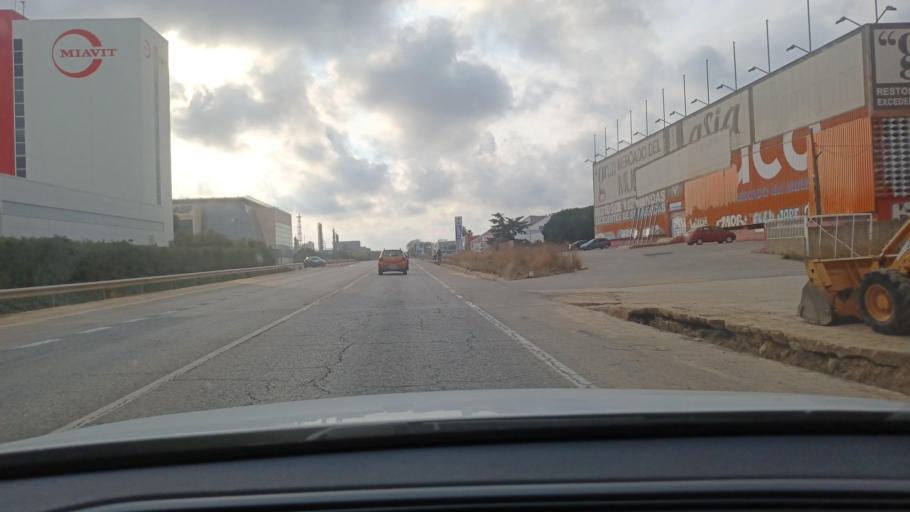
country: ES
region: Catalonia
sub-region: Provincia de Tarragona
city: Vila-seca
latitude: 41.1143
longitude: 1.1759
